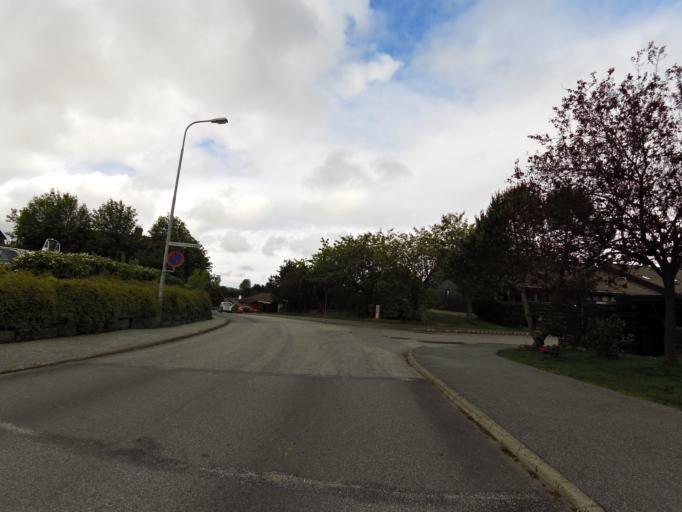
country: NO
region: Rogaland
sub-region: Stavanger
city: Stavanger
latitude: 58.9577
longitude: 5.6873
